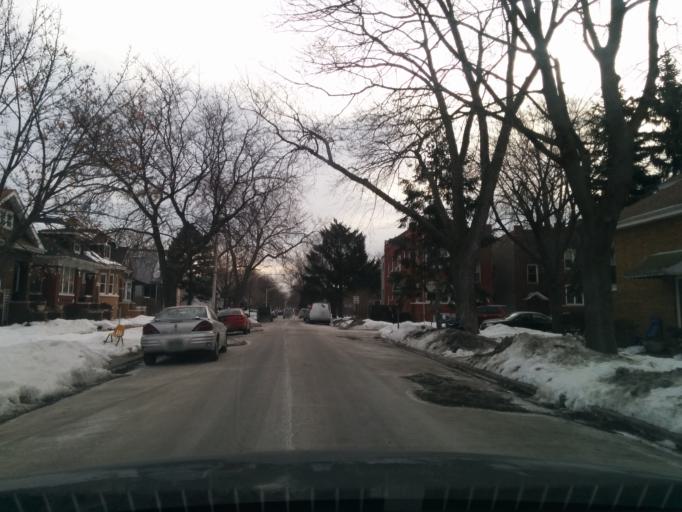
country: US
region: Illinois
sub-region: Cook County
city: Harwood Heights
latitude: 41.9478
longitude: -87.7637
